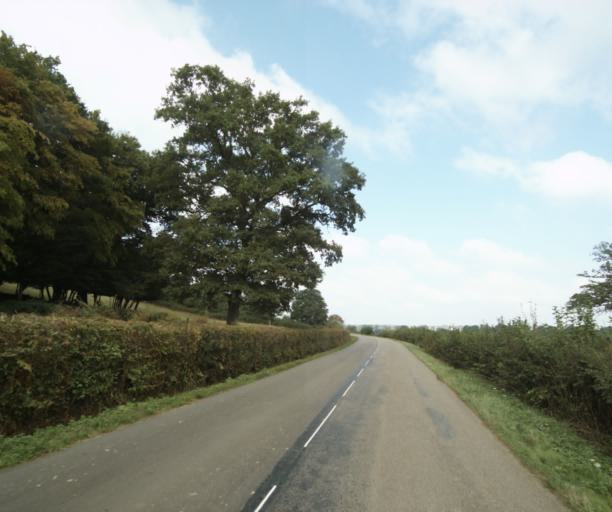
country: FR
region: Bourgogne
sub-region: Departement de Saone-et-Loire
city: Charolles
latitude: 46.4273
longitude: 4.3053
